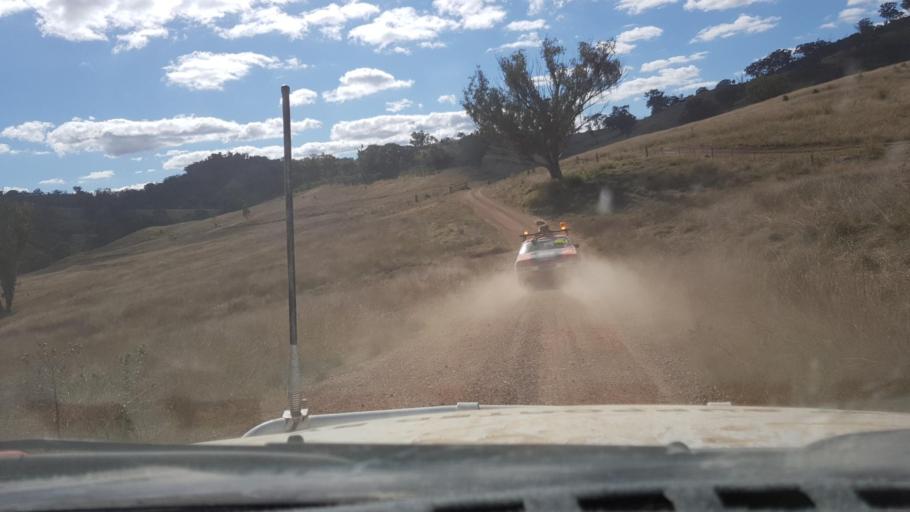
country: AU
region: New South Wales
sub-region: Tamworth Municipality
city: Manilla
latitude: -30.4408
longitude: 150.7873
